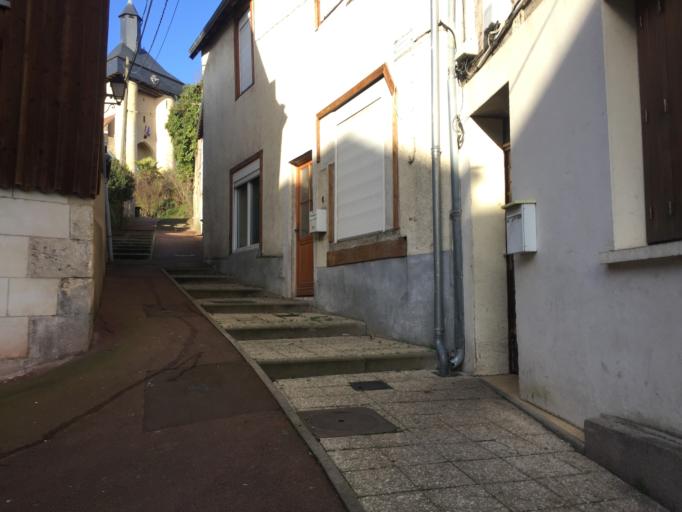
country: FR
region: Centre
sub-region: Departement d'Indre-et-Loire
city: Chateau-Renault
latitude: 47.5922
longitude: 0.9125
